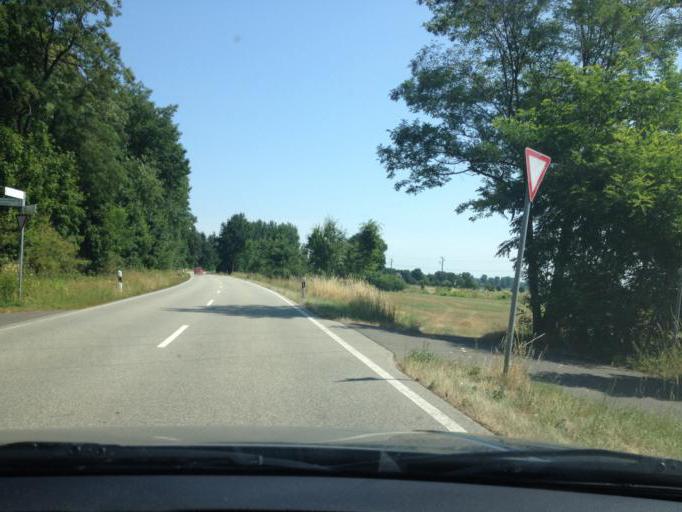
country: DE
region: Rheinland-Pfalz
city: Hutschenhausen
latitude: 49.4093
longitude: 7.4526
